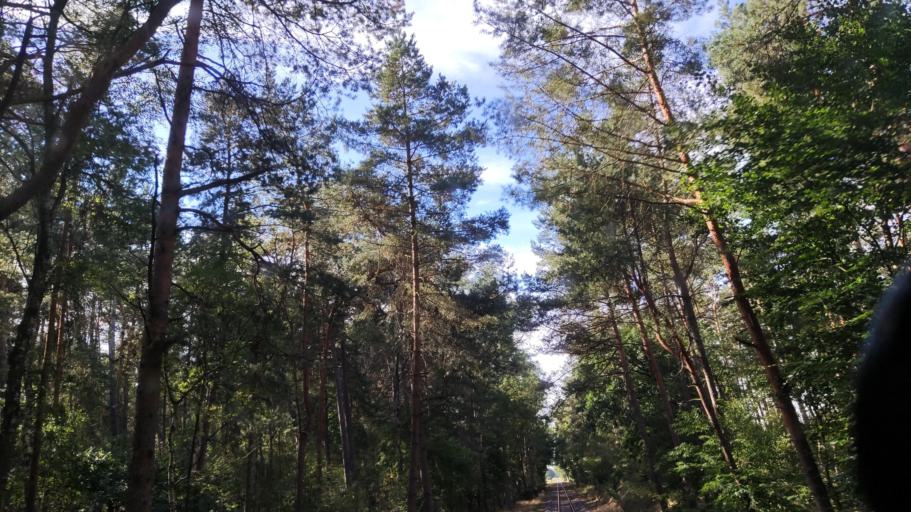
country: DE
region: Lower Saxony
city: Soltau
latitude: 53.0052
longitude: 9.8890
